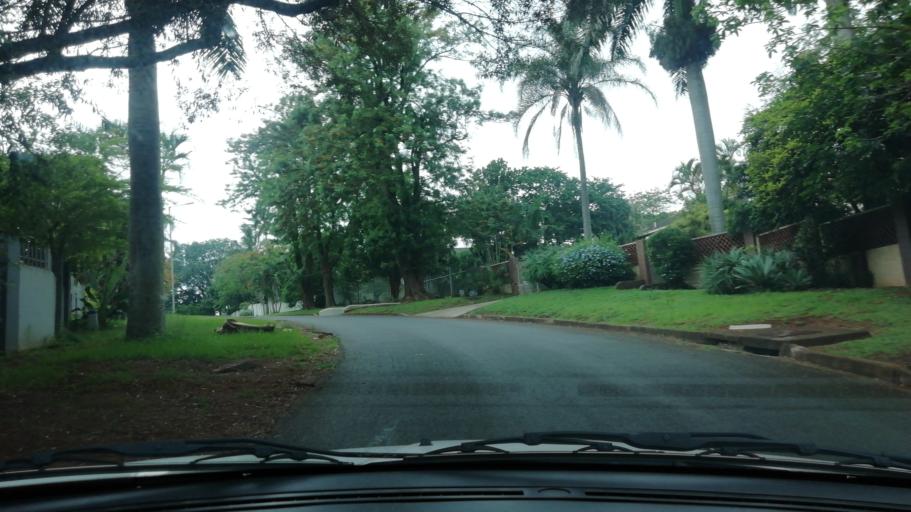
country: ZA
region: KwaZulu-Natal
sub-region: uThungulu District Municipality
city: Empangeni
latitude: -28.7605
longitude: 31.8928
